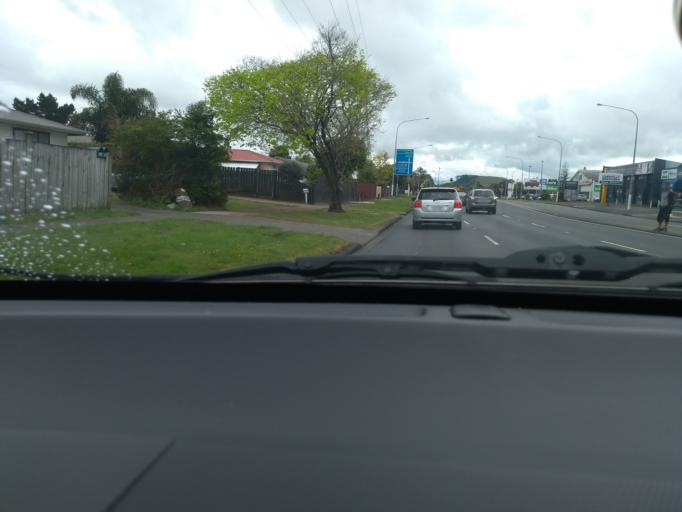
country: NZ
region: Auckland
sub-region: Auckland
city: Tamaki
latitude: -36.9166
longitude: 174.8727
